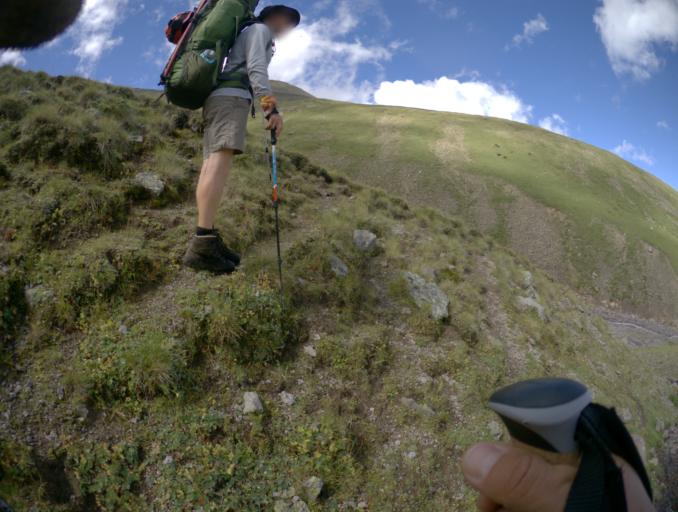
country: RU
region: Kabardino-Balkariya
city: Terskol
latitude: 43.3936
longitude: 42.3618
